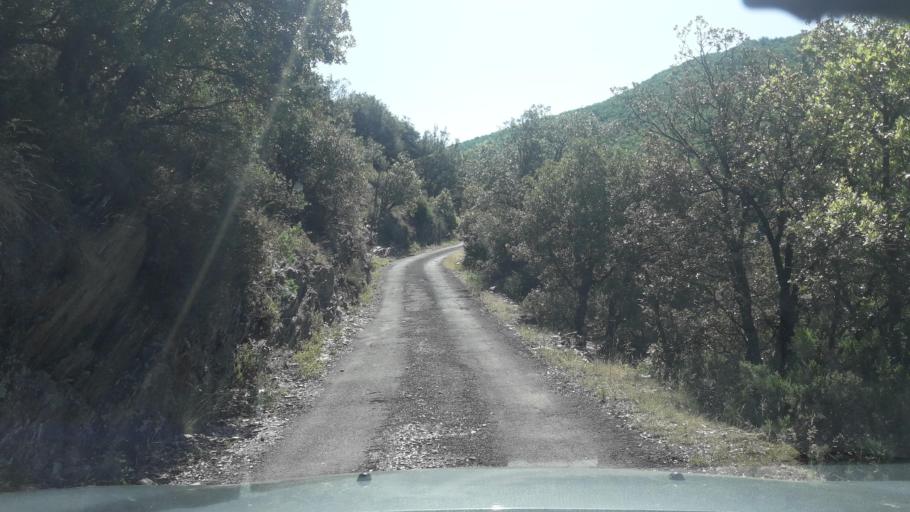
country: FR
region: Languedoc-Roussillon
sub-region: Departement du Gard
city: Valleraugue
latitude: 44.1101
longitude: 3.6945
